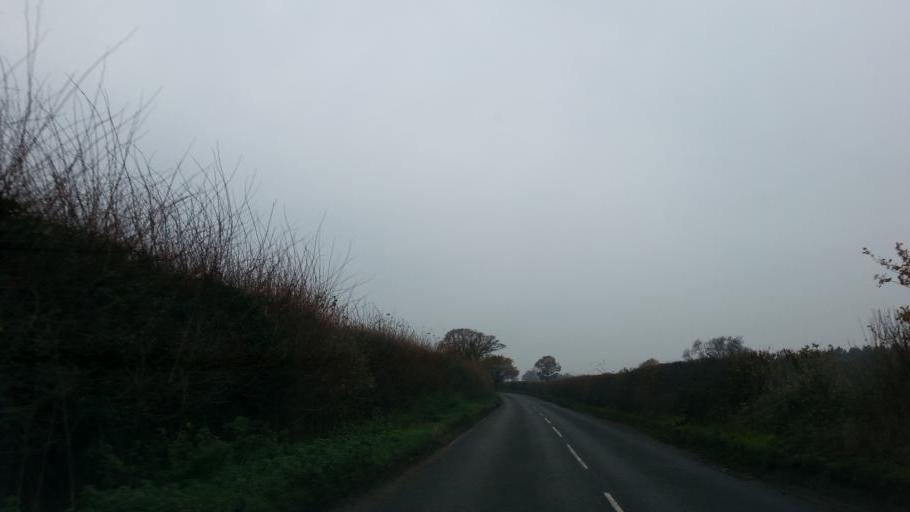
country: GB
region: England
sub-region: Suffolk
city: Thurston
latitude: 52.2475
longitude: 0.7912
